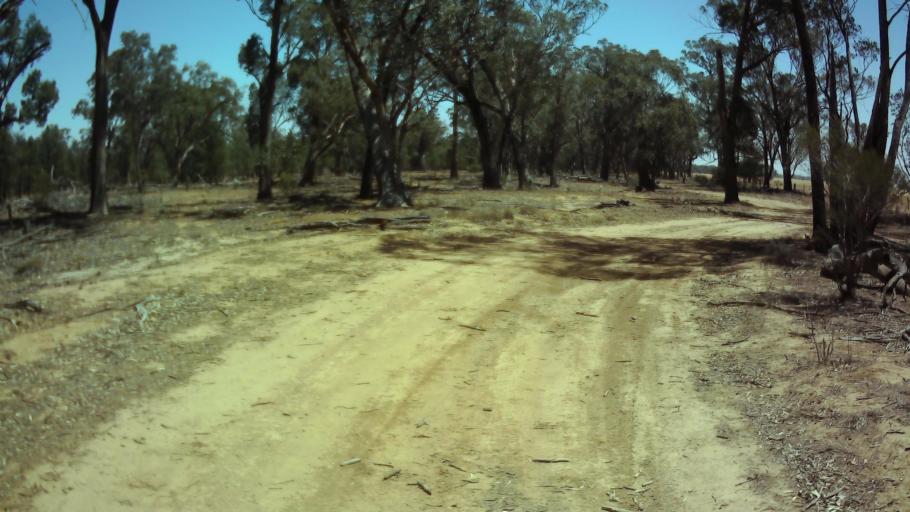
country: AU
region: New South Wales
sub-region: Weddin
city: Grenfell
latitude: -34.0619
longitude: 147.8082
